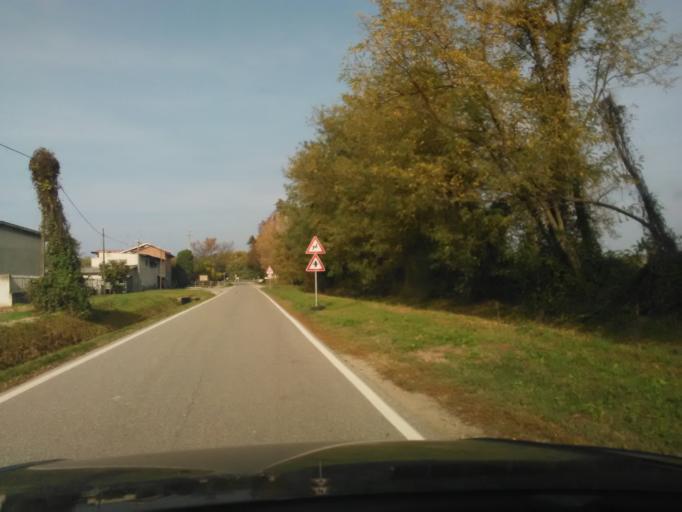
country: IT
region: Piedmont
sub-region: Provincia di Vercelli
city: Santhia
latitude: 45.3581
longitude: 8.1525
